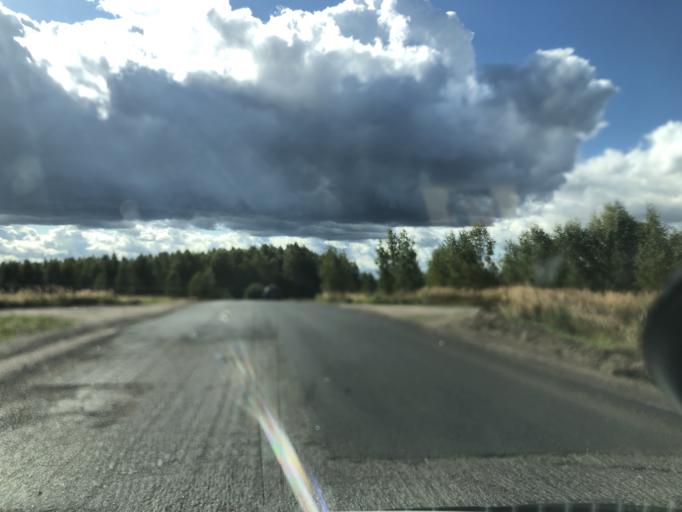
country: RU
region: Jaroslavl
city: Petrovsk
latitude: 56.9579
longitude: 39.3535
